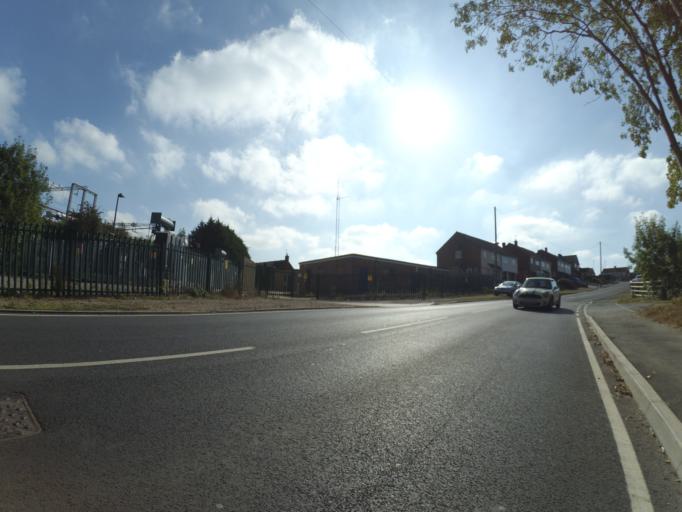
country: GB
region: England
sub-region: Warwickshire
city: Rugby
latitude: 52.3668
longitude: -1.2208
